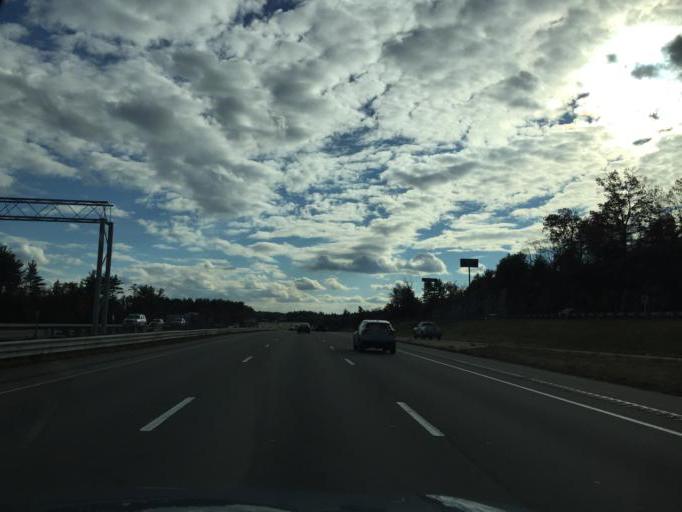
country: US
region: Massachusetts
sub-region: Middlesex County
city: Tyngsboro
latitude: 42.7139
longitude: -71.4501
